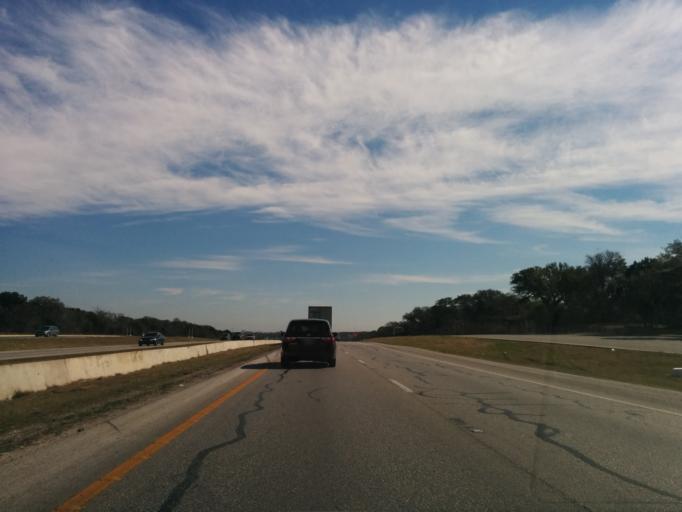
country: US
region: Texas
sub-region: Bexar County
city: Shavano Park
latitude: 29.6012
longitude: -98.5550
